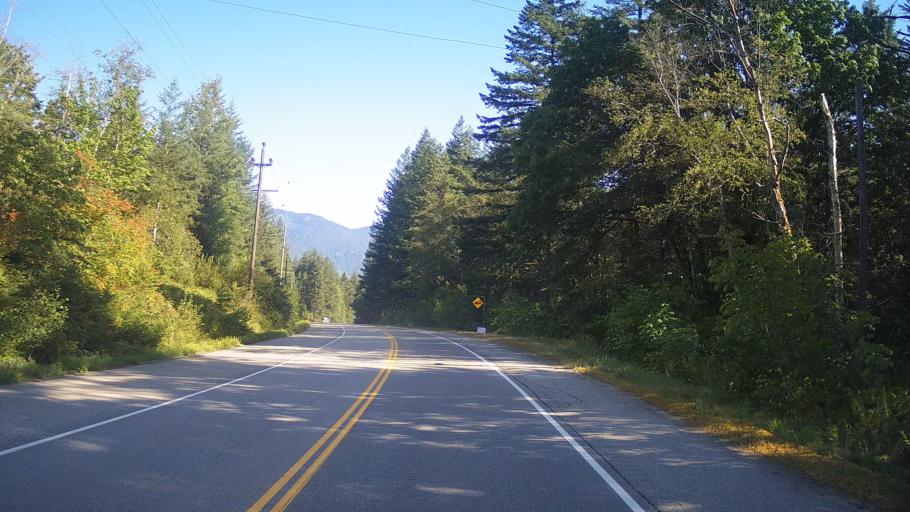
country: CA
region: British Columbia
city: Hope
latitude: 49.5126
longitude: -121.4183
